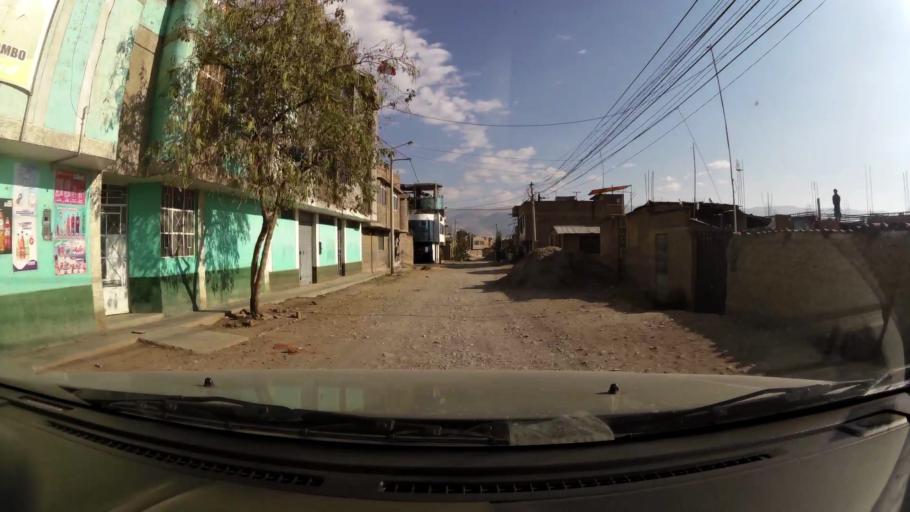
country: PE
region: Junin
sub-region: Provincia de Huancayo
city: El Tambo
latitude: -12.0586
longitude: -75.2290
